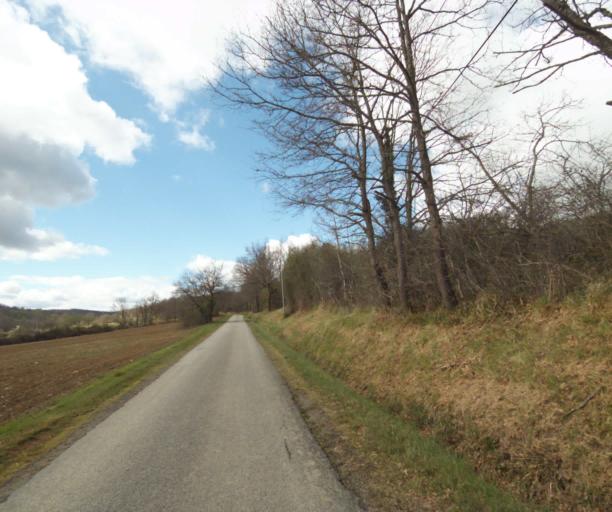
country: FR
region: Midi-Pyrenees
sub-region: Departement de l'Ariege
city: Saverdun
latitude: 43.1997
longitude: 1.5692
